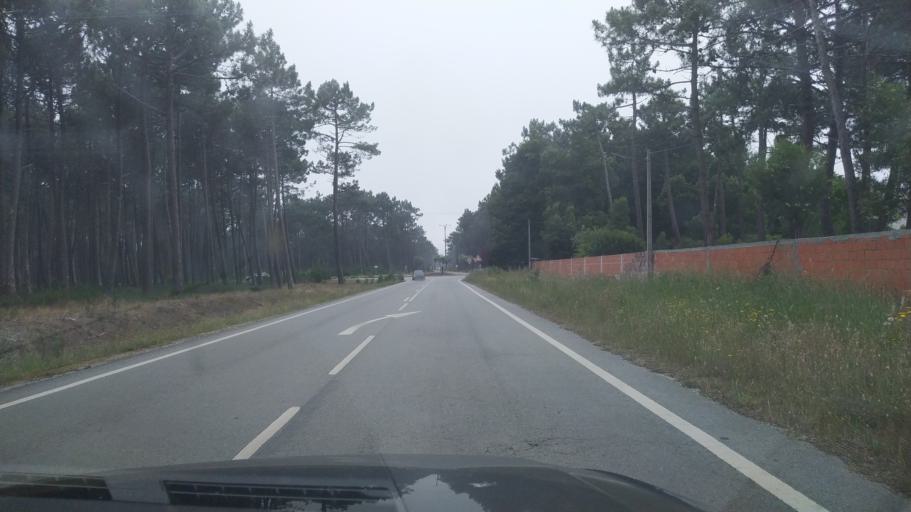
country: PT
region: Aveiro
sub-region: Ilhavo
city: Gafanha da Encarnacao
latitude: 40.5874
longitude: -8.7292
